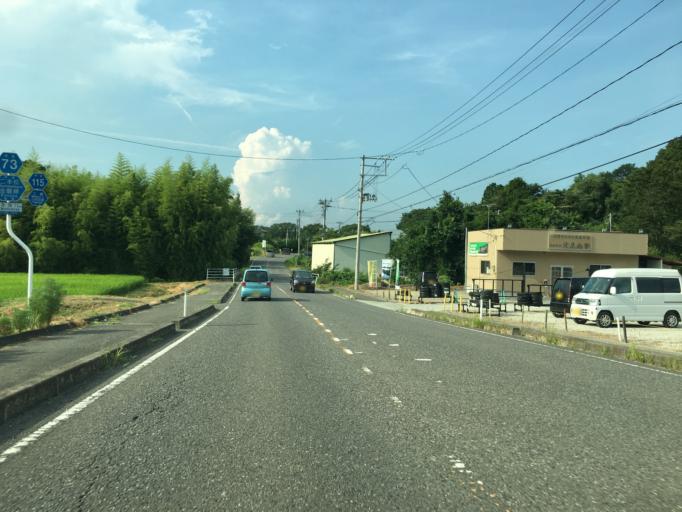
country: JP
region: Fukushima
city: Miharu
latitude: 37.4481
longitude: 140.4275
